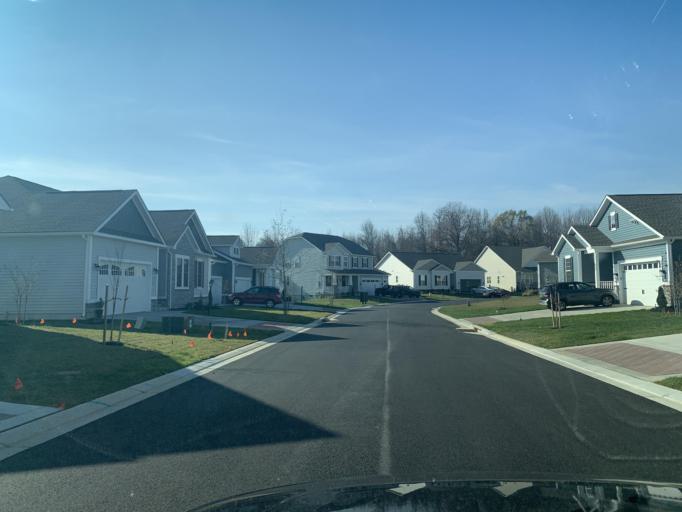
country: US
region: Maryland
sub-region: Harford County
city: Havre de Grace
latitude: 39.5398
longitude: -76.1161
